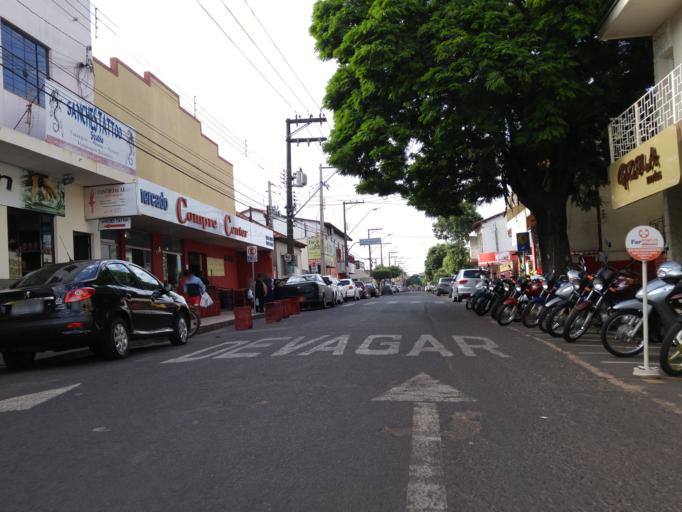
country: BR
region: Sao Paulo
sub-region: Paraguacu Paulista
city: Paraguacu Paulista
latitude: -22.4161
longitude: -50.5776
